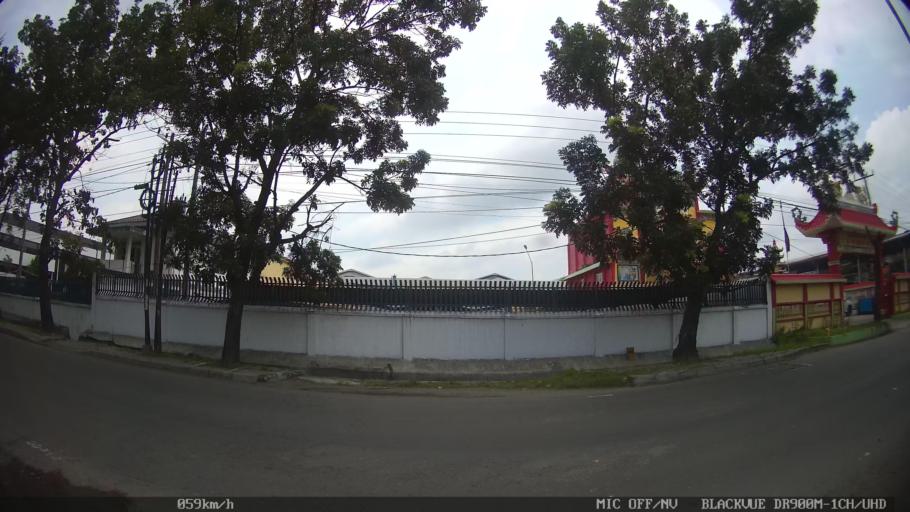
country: ID
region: North Sumatra
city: Medan
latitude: 3.6547
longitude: 98.6637
